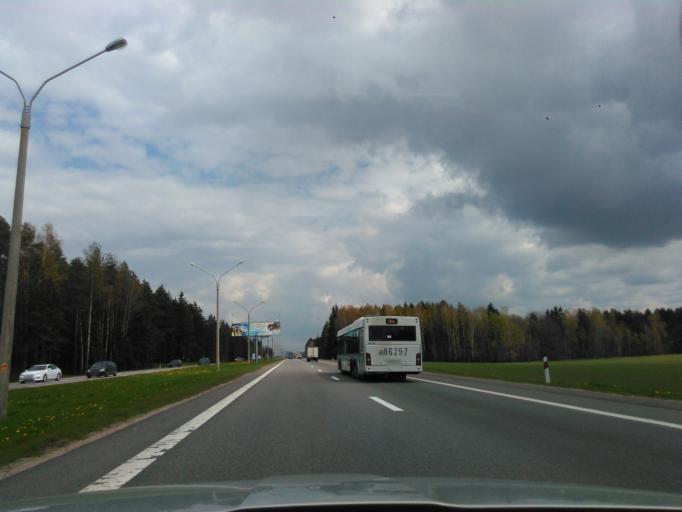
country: BY
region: Minsk
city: Korolev Stan
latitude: 54.0020
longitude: 27.8358
